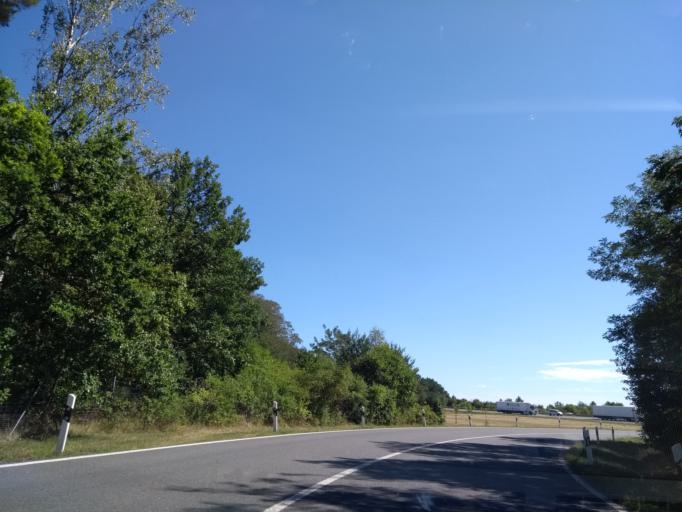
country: DE
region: Brandenburg
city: Bronkow
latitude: 51.6648
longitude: 13.9133
